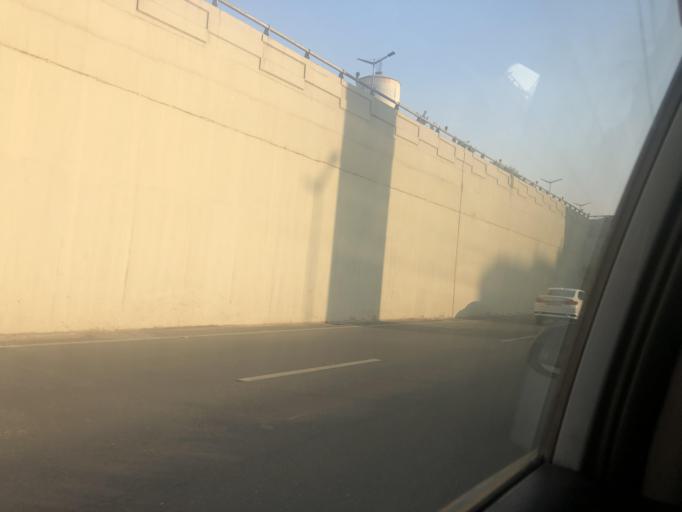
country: IN
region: Haryana
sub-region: Gurgaon
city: Gurgaon
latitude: 28.4694
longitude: 77.0942
